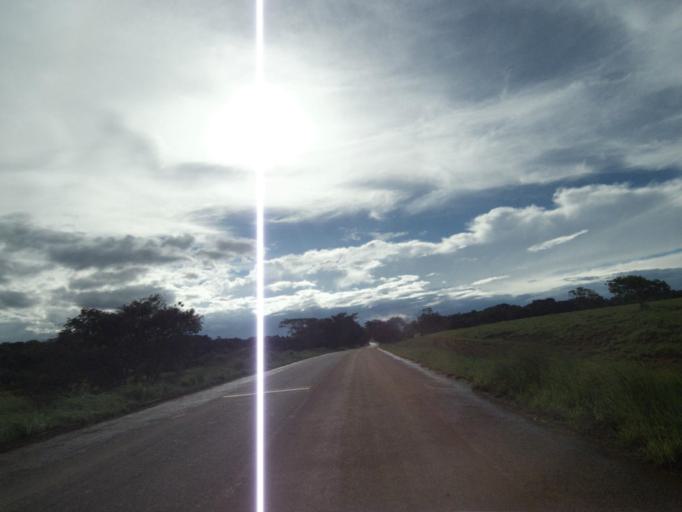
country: BR
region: Goias
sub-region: Itaberai
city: Itaberai
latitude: -15.9084
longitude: -49.5636
